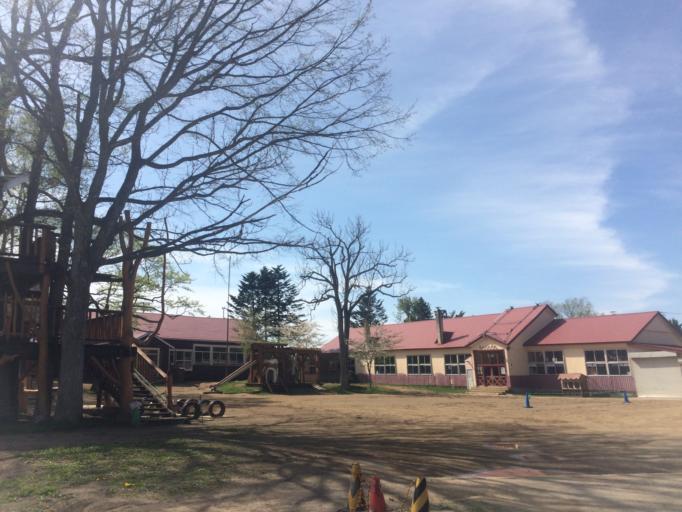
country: JP
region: Hokkaido
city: Niseko Town
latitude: 42.9055
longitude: 140.7561
